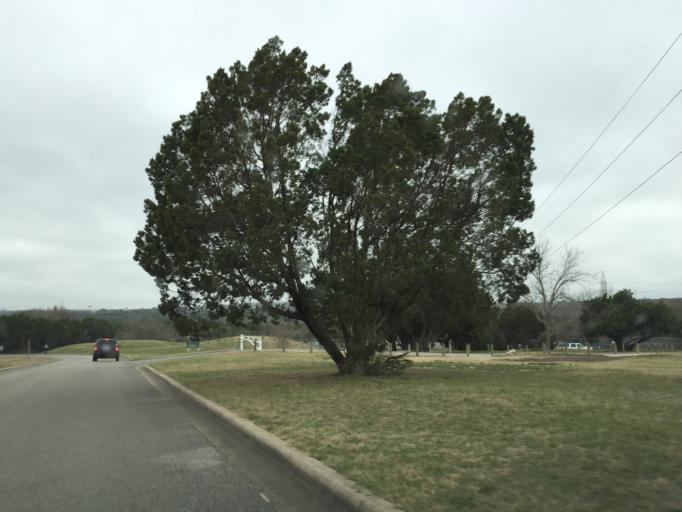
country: US
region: Texas
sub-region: Travis County
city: Wells Branch
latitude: 30.4044
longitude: -97.6866
